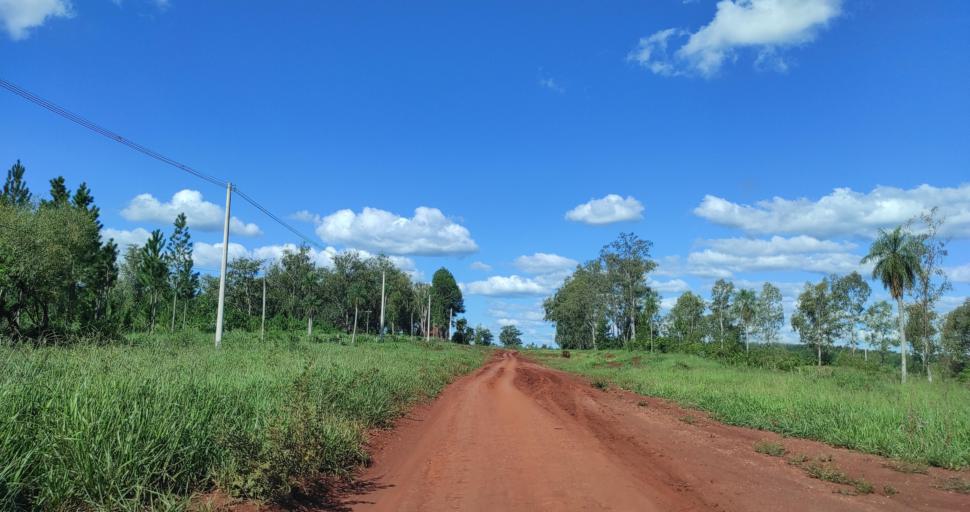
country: AR
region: Misiones
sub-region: Departamento de Candelaria
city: Candelaria
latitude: -27.4646
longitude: -55.7157
